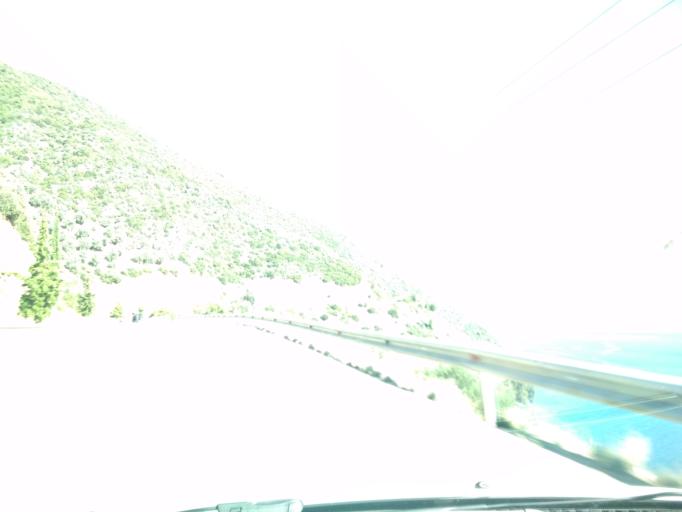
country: GR
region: Central Greece
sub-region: Nomos Evvoias
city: Oreoi
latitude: 38.8495
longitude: 23.0620
